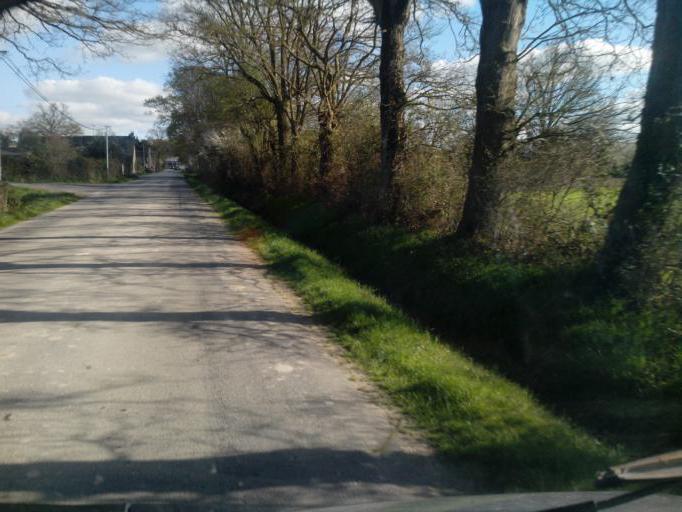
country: FR
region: Brittany
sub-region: Departement d'Ille-et-Vilaine
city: Messac
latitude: 47.7863
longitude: -1.7870
